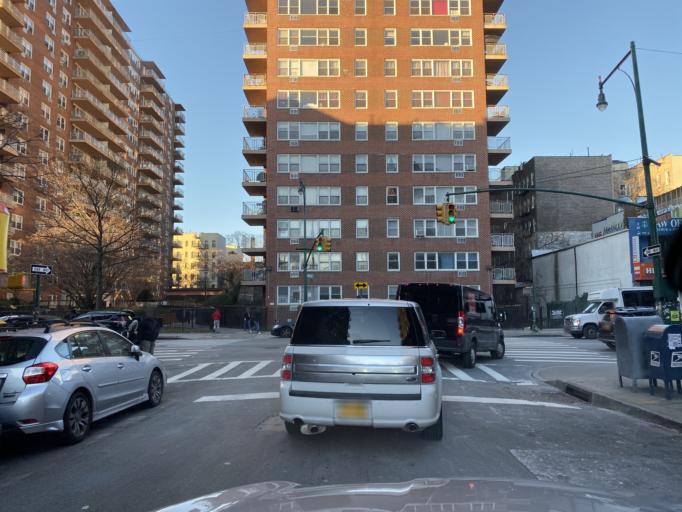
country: US
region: New York
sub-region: Kings County
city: Brooklyn
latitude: 40.6595
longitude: -73.9603
